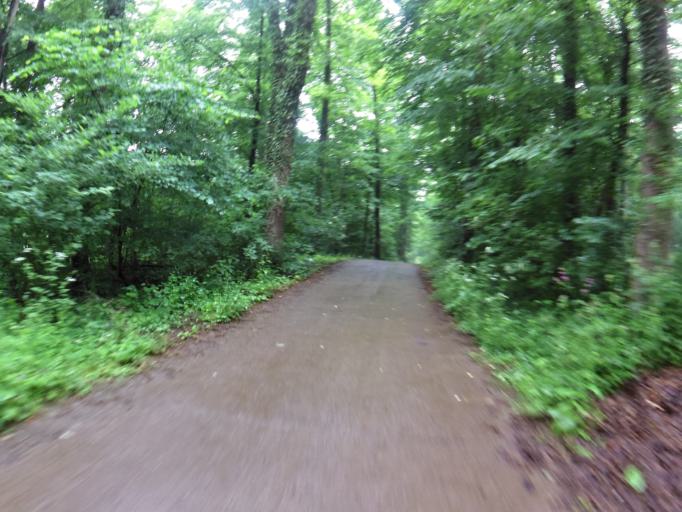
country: DE
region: Hesse
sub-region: Regierungsbezirk Kassel
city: Bad Hersfeld
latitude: 50.8827
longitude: 9.7304
